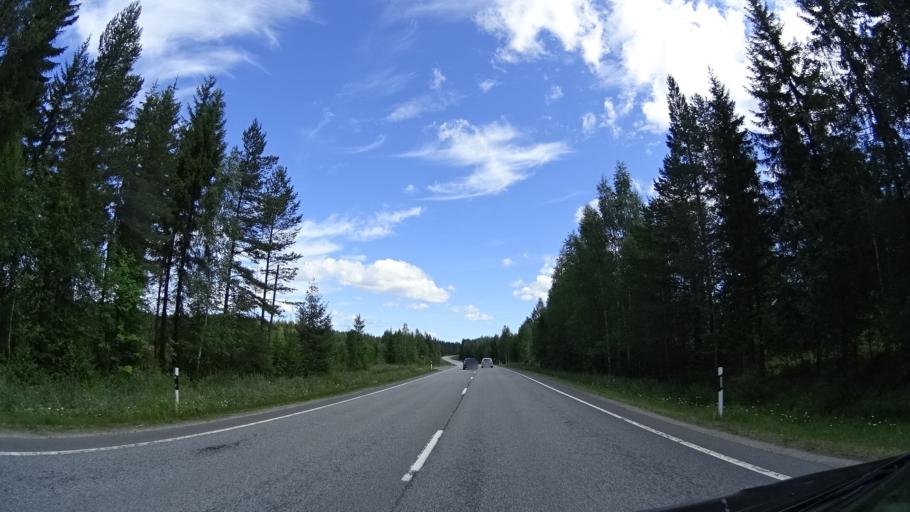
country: FI
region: Pirkanmaa
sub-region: Luoteis-Pirkanmaa
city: Kihnioe
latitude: 62.1379
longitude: 23.1440
